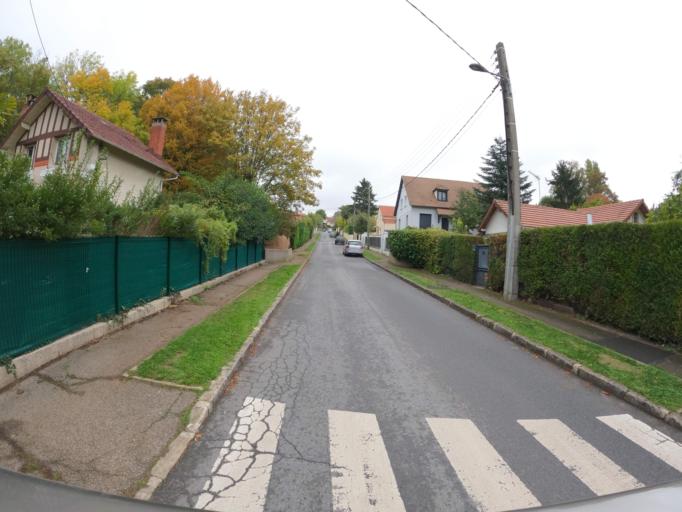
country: FR
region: Ile-de-France
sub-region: Departement du Val-de-Marne
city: Sucy-en-Brie
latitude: 48.7772
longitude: 2.5185
